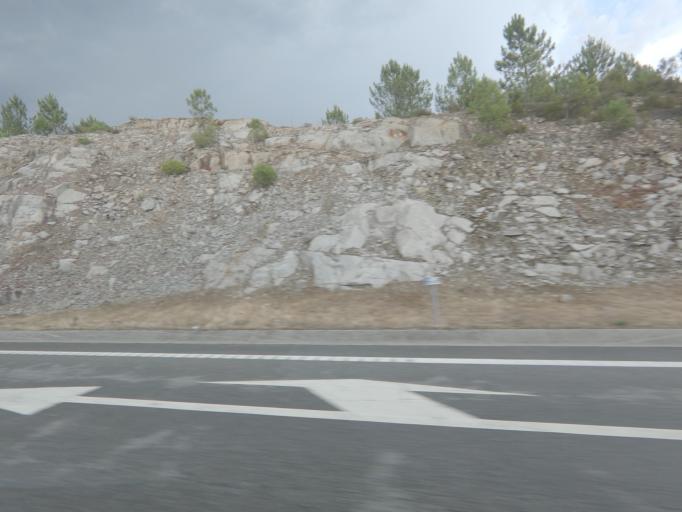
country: PT
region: Viseu
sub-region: Viseu
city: Abraveses
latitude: 40.6746
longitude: -7.9682
